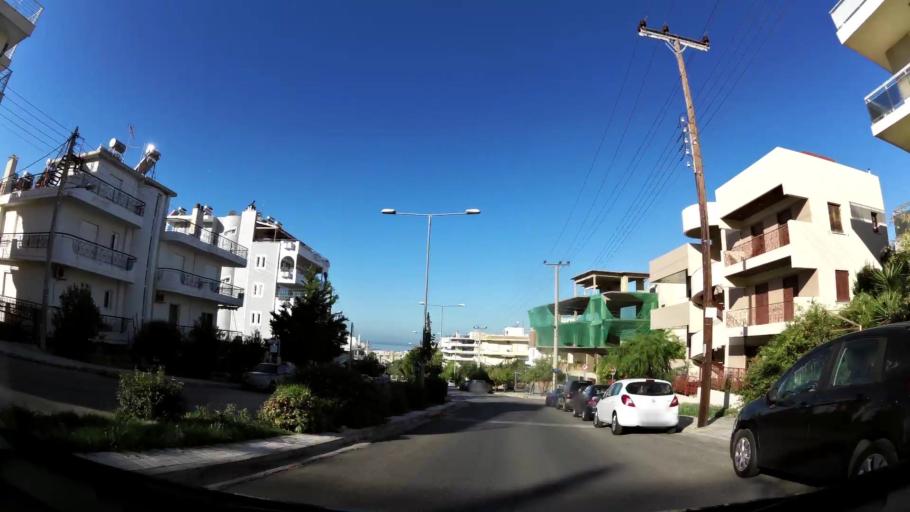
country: GR
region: Attica
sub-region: Nomarchia Athinas
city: Glyfada
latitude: 37.8746
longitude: 23.7689
